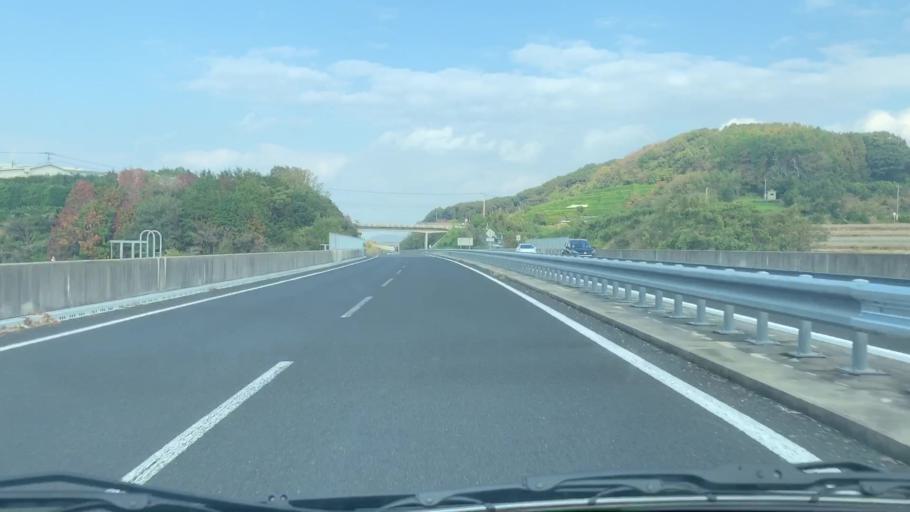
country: JP
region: Nagasaki
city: Sasebo
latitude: 33.0459
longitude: 129.7500
